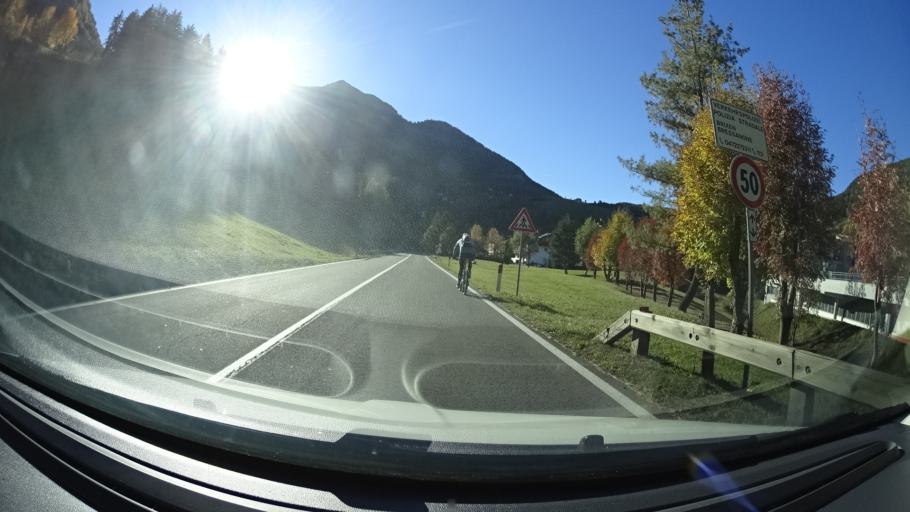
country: IT
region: Trentino-Alto Adige
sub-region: Bolzano
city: Ortisei
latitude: 46.5734
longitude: 11.6522
